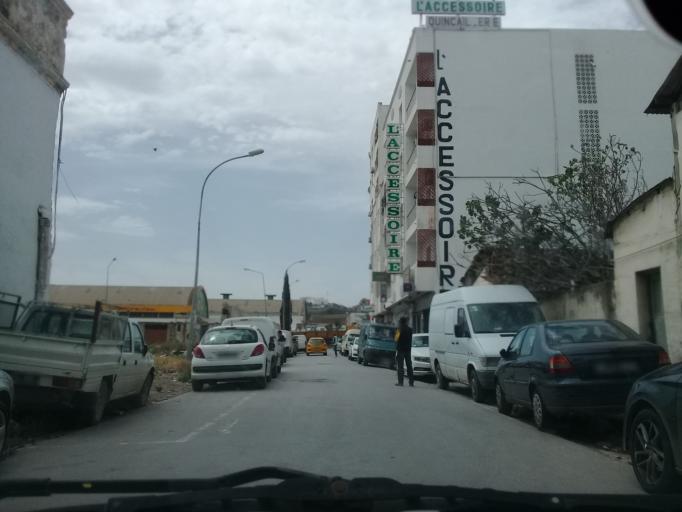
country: TN
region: Tunis
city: Tunis
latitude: 36.7916
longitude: 10.1836
